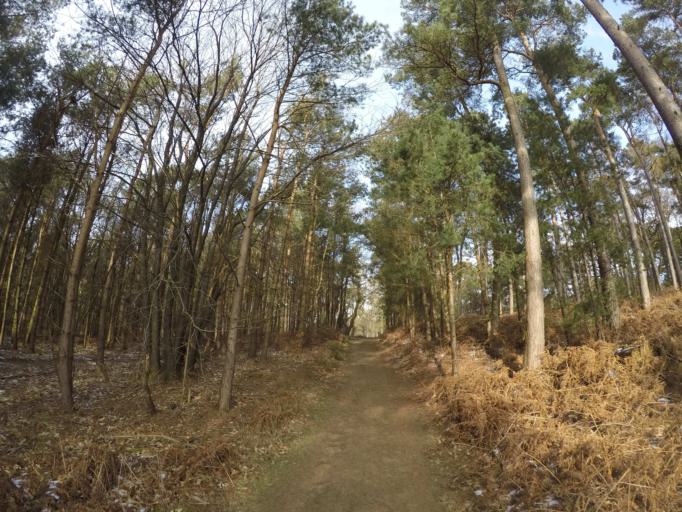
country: GB
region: England
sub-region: Milton Keynes
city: Bow Brickhill
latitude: 51.9943
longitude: -0.6756
